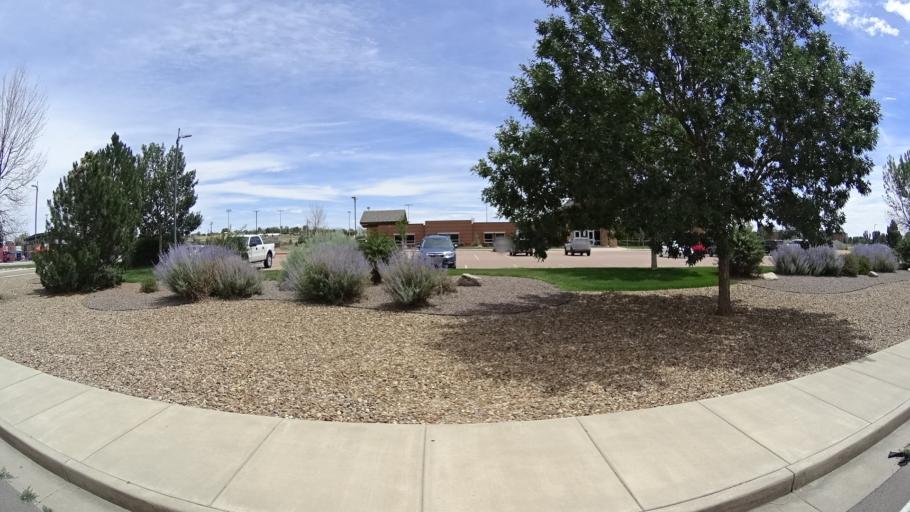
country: US
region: Colorado
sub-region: El Paso County
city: Fountain
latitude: 38.6757
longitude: -104.6873
